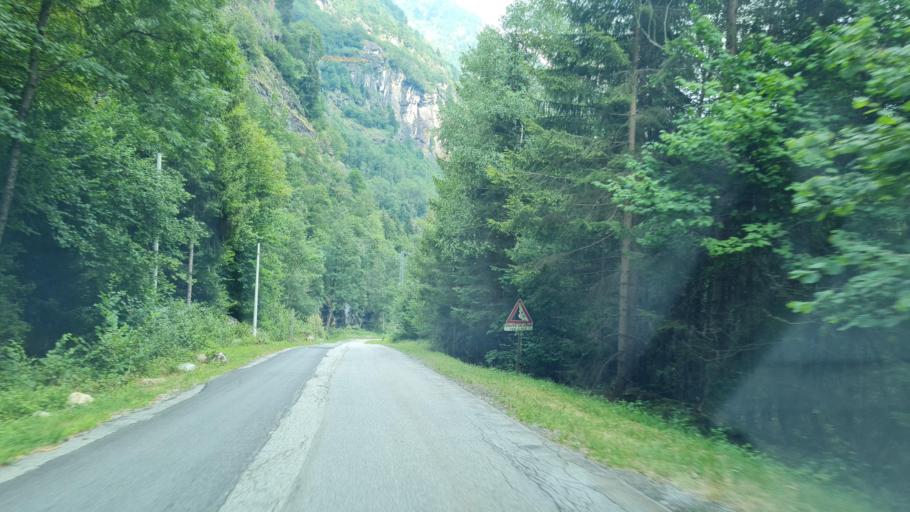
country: IT
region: Piedmont
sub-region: Provincia Verbano-Cusio-Ossola
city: Baceno
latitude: 46.2877
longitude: 8.2786
